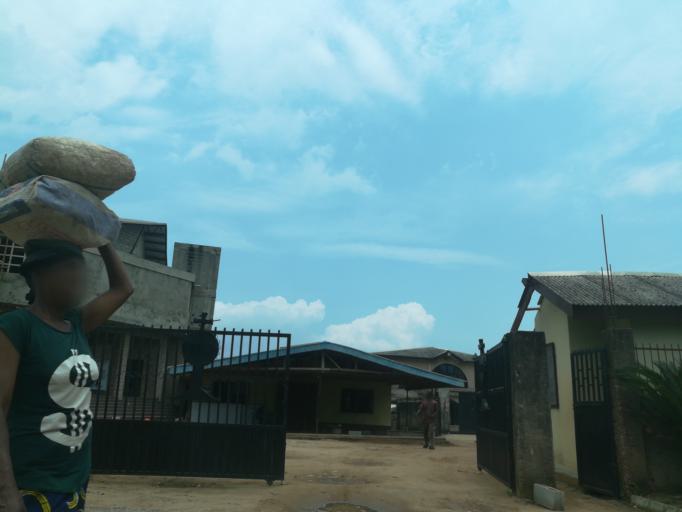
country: NG
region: Lagos
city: Ikorodu
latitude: 6.5633
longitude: 3.6036
